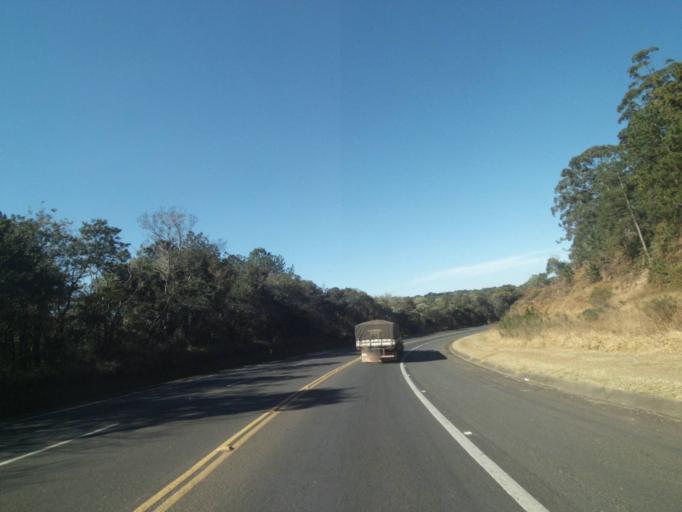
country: BR
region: Parana
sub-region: Reserva
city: Reserva
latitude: -24.6393
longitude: -50.6276
